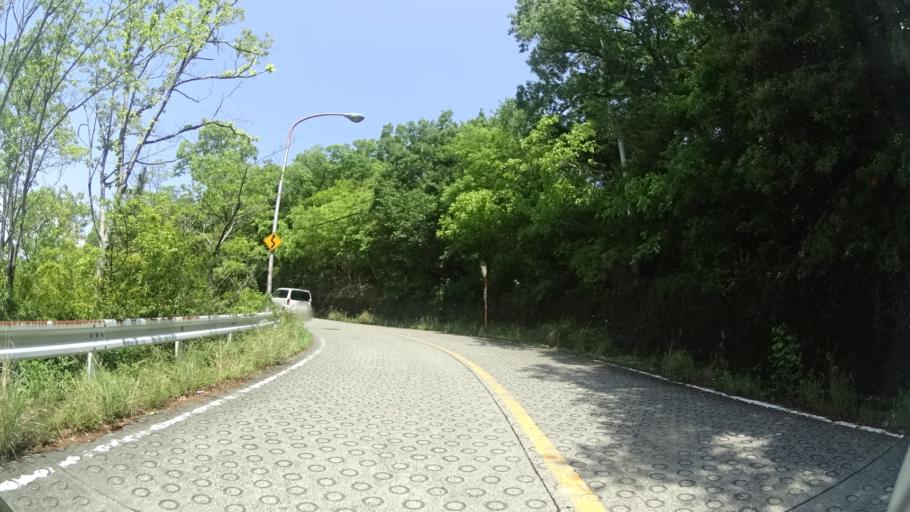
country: JP
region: Tokushima
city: Tokushima-shi
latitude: 34.0609
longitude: 134.5416
